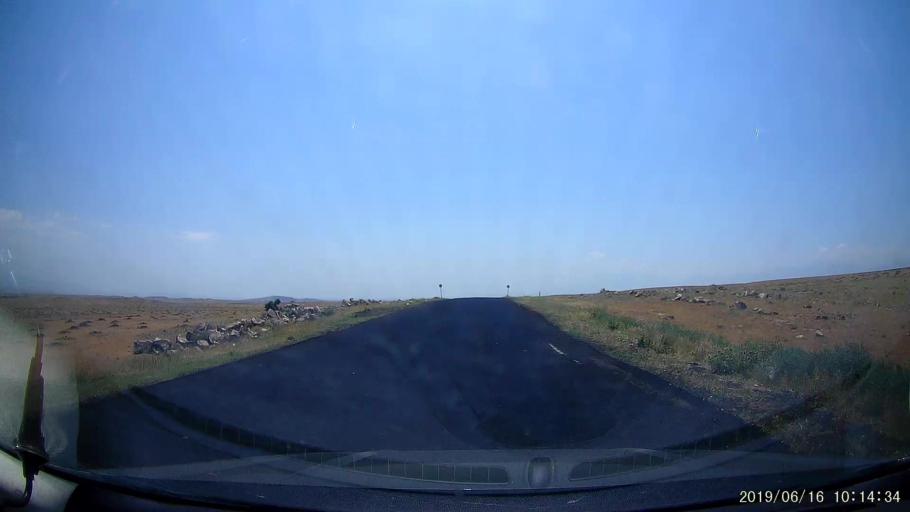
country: TR
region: Igdir
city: Tuzluca
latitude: 40.1836
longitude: 43.6656
